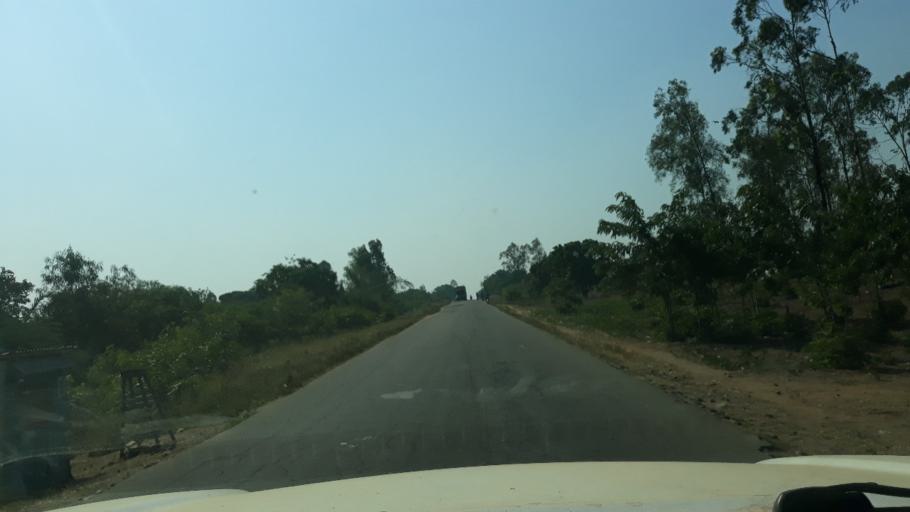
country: BI
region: Cibitoke
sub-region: Commune of Buganda
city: Buganda
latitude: -3.0688
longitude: 29.1214
